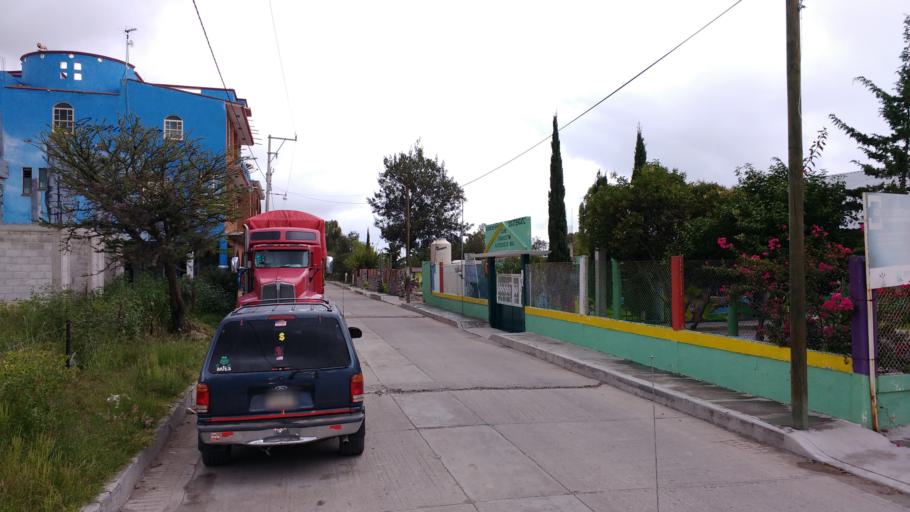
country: MX
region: Hidalgo
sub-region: Tezontepec de Aldama
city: Tenango
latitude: 20.2753
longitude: -99.2754
